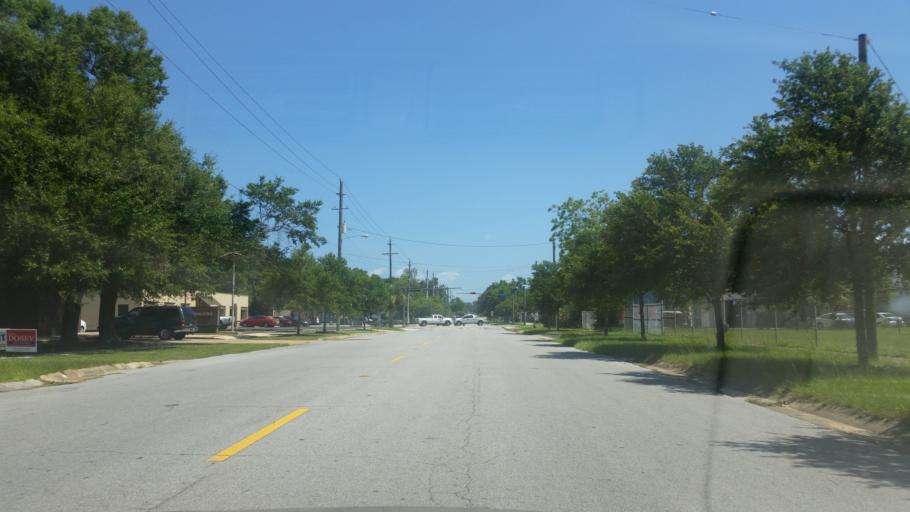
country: US
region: Florida
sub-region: Escambia County
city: Pensacola
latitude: 30.4100
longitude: -87.2261
